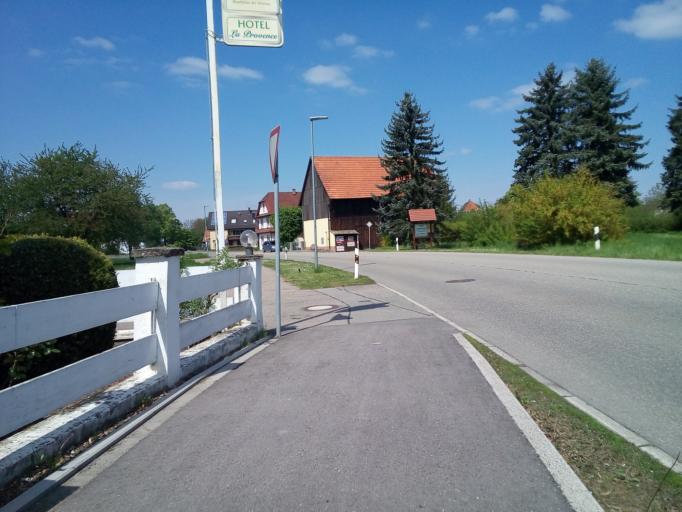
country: DE
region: Baden-Wuerttemberg
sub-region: Freiburg Region
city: Rheinau
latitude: 48.6471
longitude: 7.8958
